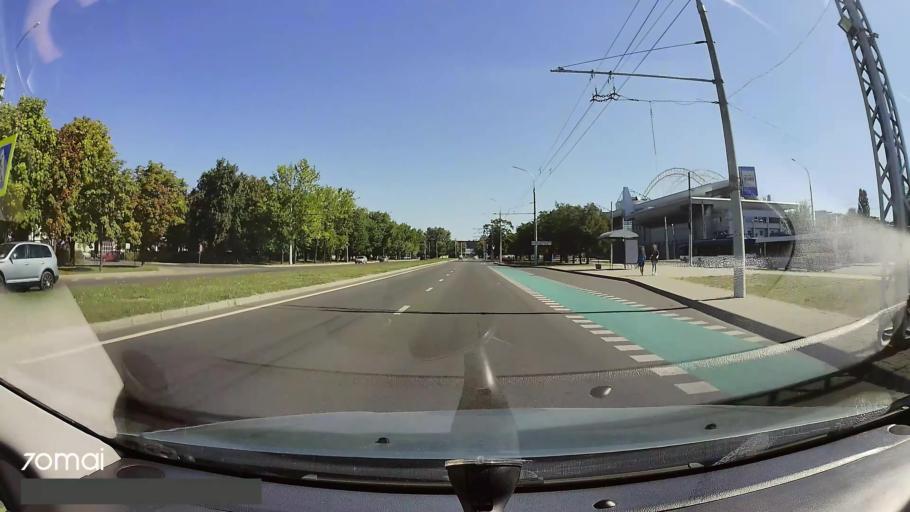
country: BY
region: Brest
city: Brest
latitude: 52.1143
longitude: 23.7753
